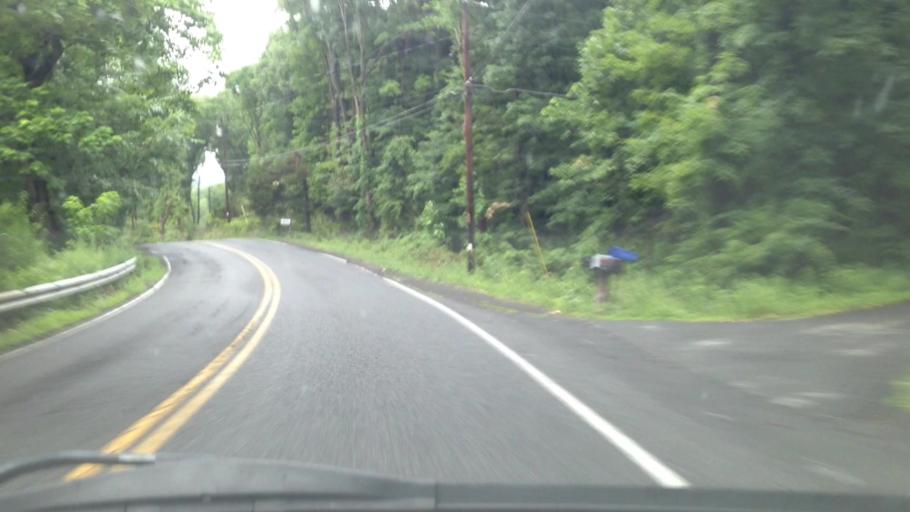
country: US
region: New York
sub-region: Ulster County
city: New Paltz
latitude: 41.7744
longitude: -74.0570
